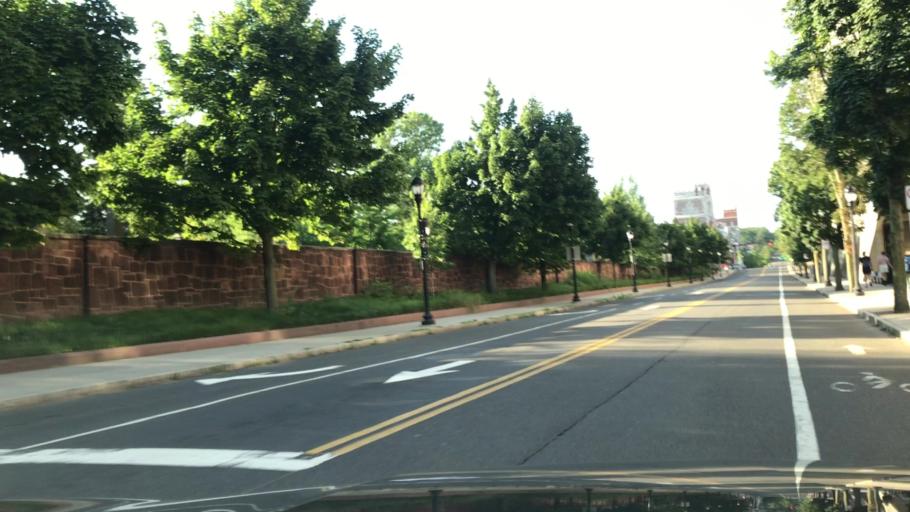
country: US
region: Connecticut
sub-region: New Haven County
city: New Haven
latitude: 41.3118
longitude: -72.9256
